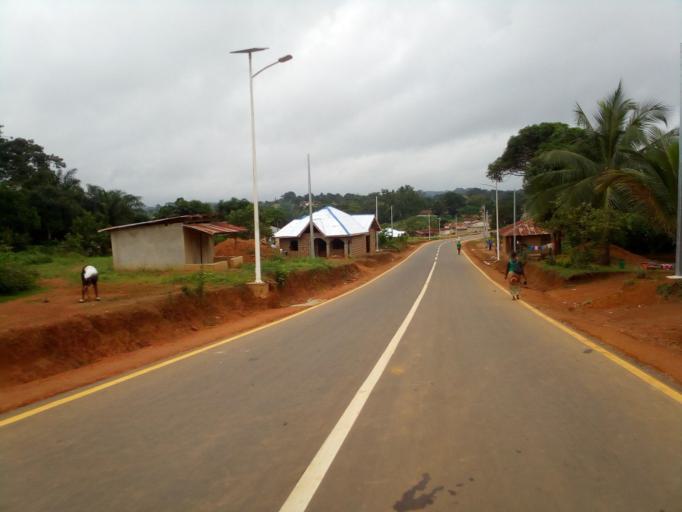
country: SL
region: Eastern Province
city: Kailahun
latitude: 8.2719
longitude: -10.5791
